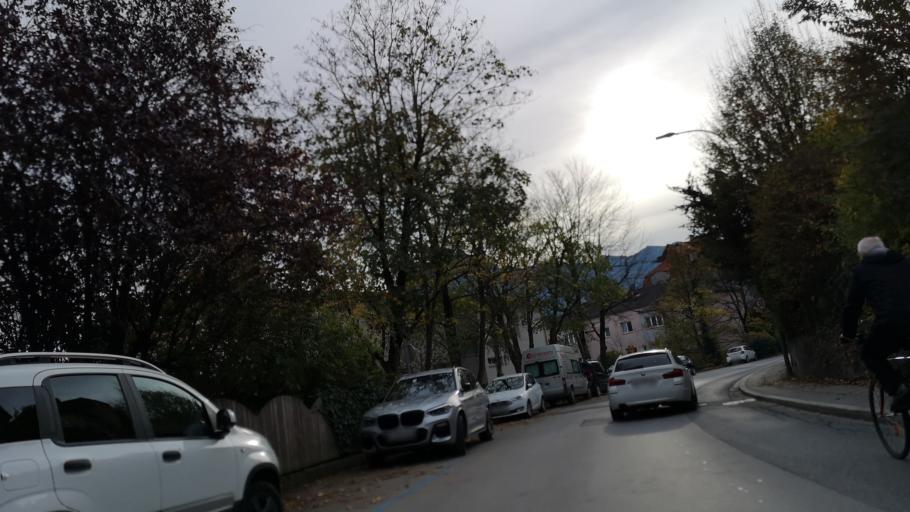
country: AT
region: Tyrol
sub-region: Innsbruck Stadt
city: Innsbruck
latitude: 47.2684
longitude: 11.3826
